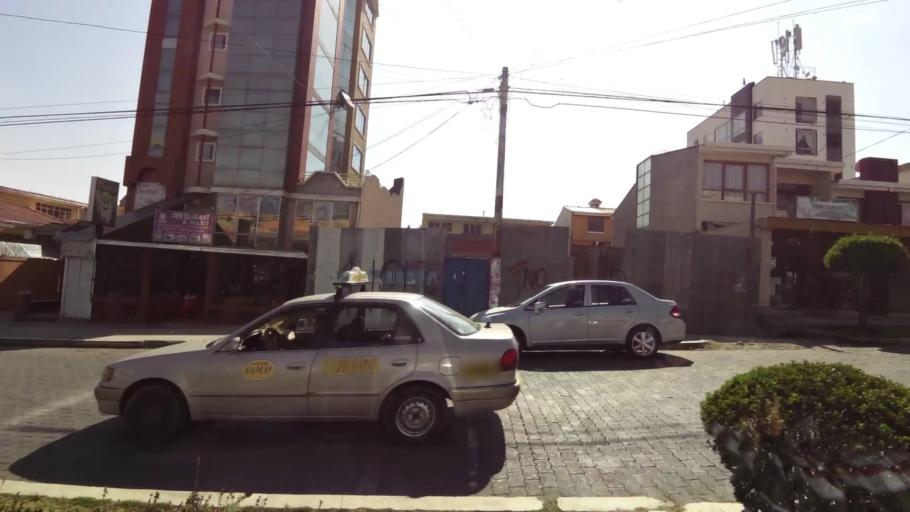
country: BO
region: La Paz
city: La Paz
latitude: -16.5330
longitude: -68.0743
